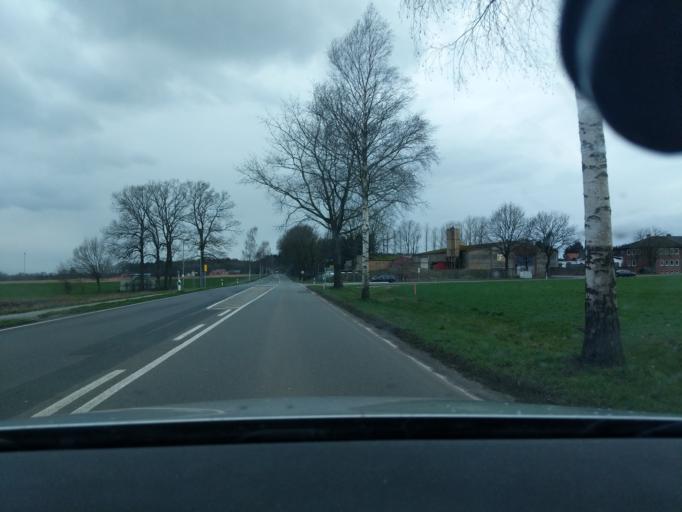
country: DE
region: Lower Saxony
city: Kutenholz
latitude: 53.4914
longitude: 9.3080
